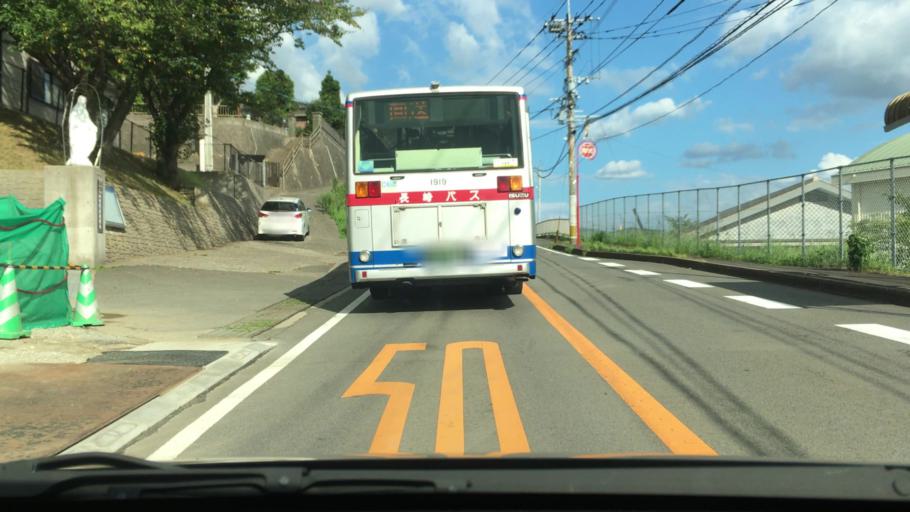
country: JP
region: Nagasaki
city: Togitsu
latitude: 32.8244
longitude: 129.7567
